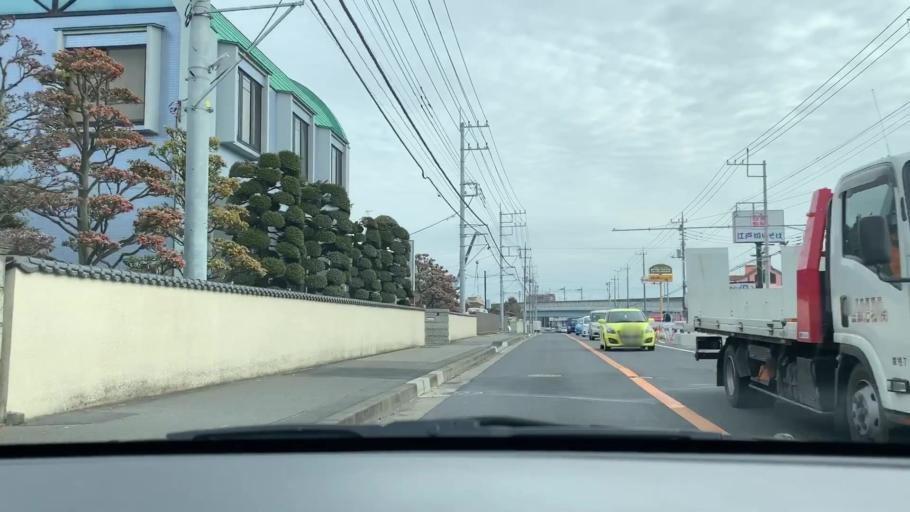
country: JP
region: Chiba
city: Kashiwa
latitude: 35.8878
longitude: 139.9465
